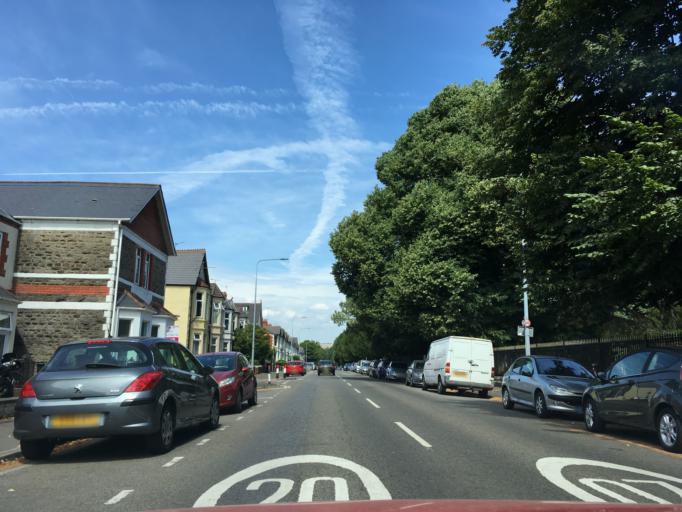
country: GB
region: Wales
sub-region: Cardiff
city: Cardiff
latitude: 51.5008
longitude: -3.1839
